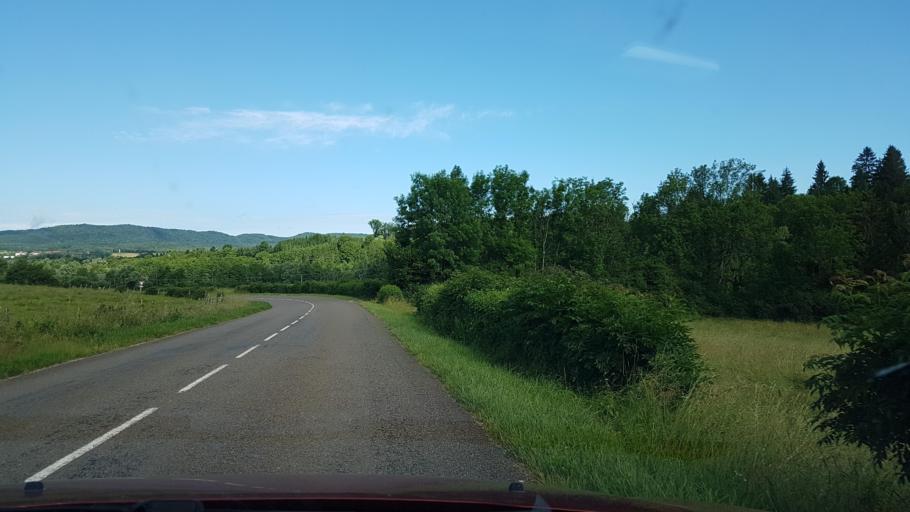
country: FR
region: Franche-Comte
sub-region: Departement du Jura
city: Clairvaux-les-Lacs
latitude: 46.5938
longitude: 5.7301
